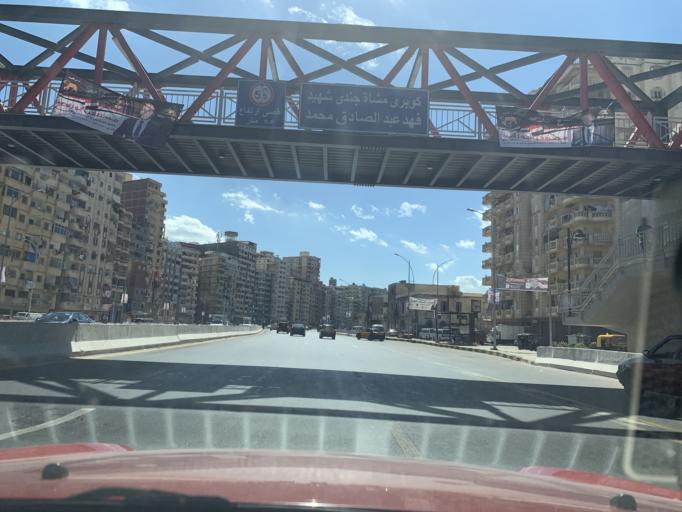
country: EG
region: Alexandria
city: Alexandria
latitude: 31.1997
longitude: 29.9356
